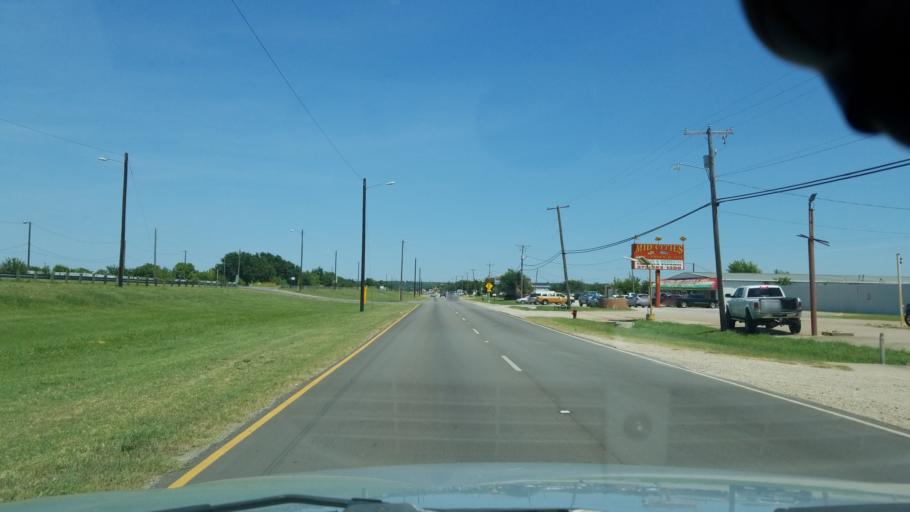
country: US
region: Texas
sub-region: Dallas County
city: Grand Prairie
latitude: 32.7463
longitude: -96.9490
